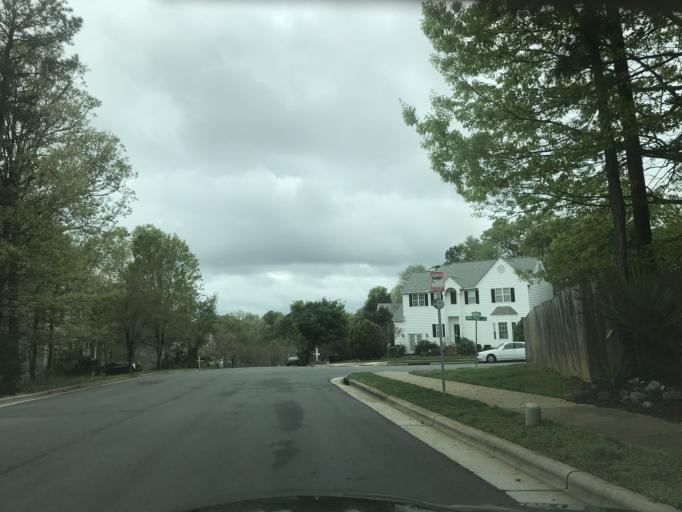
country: US
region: North Carolina
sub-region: Wake County
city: West Raleigh
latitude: 35.7467
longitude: -78.6844
